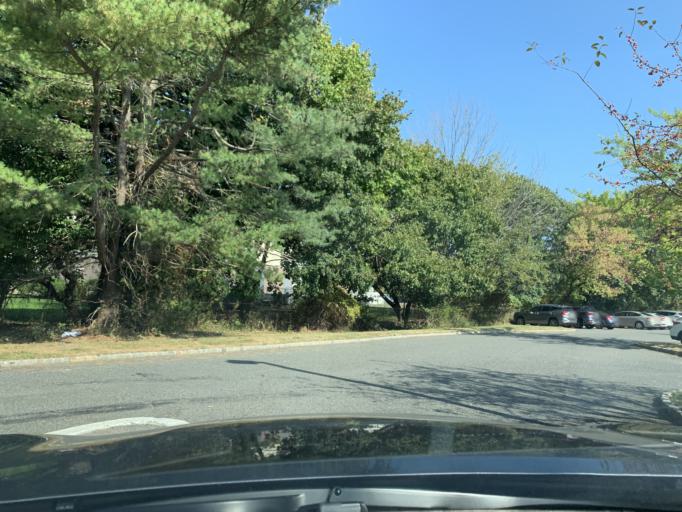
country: US
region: New Jersey
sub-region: Monmouth County
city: Shrewsbury
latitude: 40.3137
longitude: -74.0635
